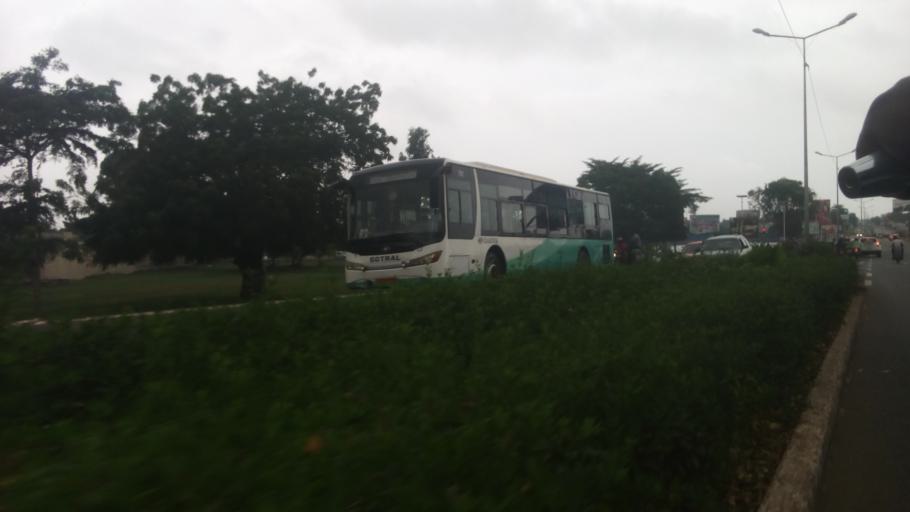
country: TG
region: Maritime
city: Lome
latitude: 6.1687
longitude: 1.2212
